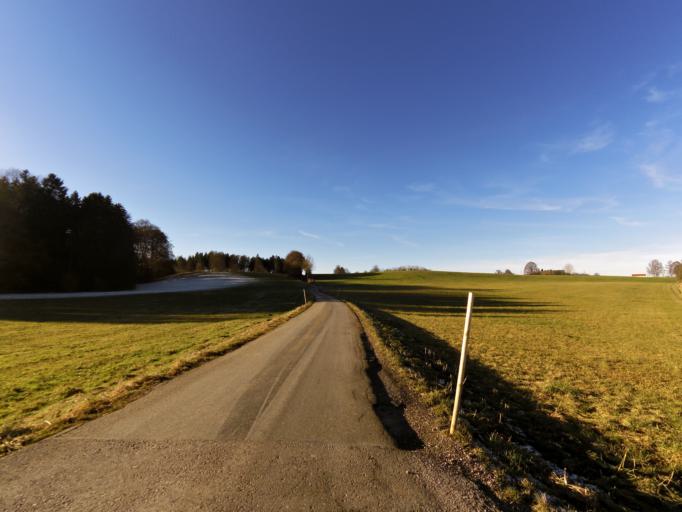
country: DE
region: Bavaria
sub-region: Upper Bavaria
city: Schaftlarn
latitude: 47.9835
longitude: 11.4418
